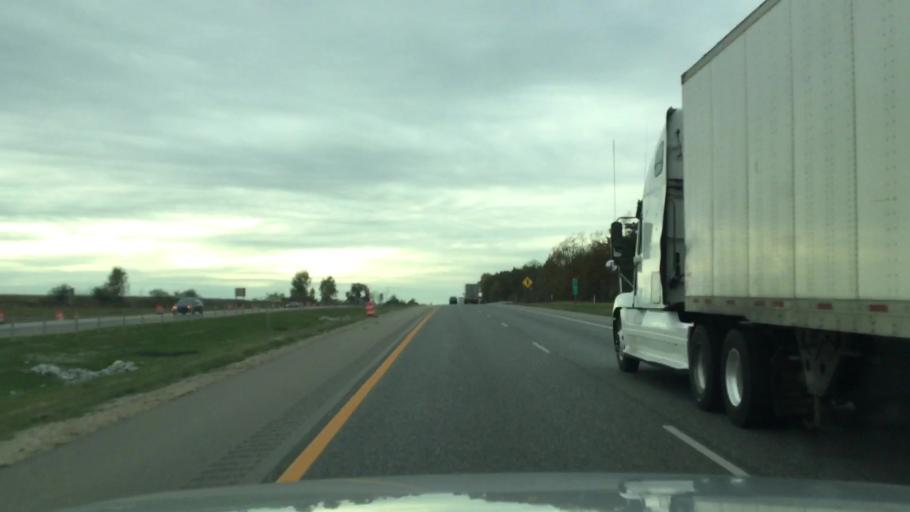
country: US
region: Michigan
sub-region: Van Buren County
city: Hartford
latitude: 42.1967
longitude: -86.0530
